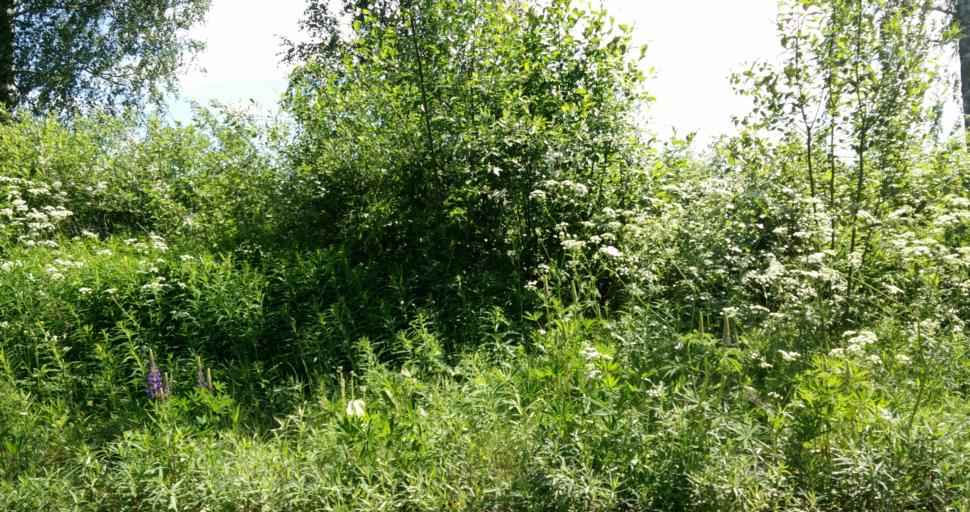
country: SE
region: Vaermland
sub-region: Hagfors Kommun
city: Hagfors
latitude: 60.0014
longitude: 13.6051
